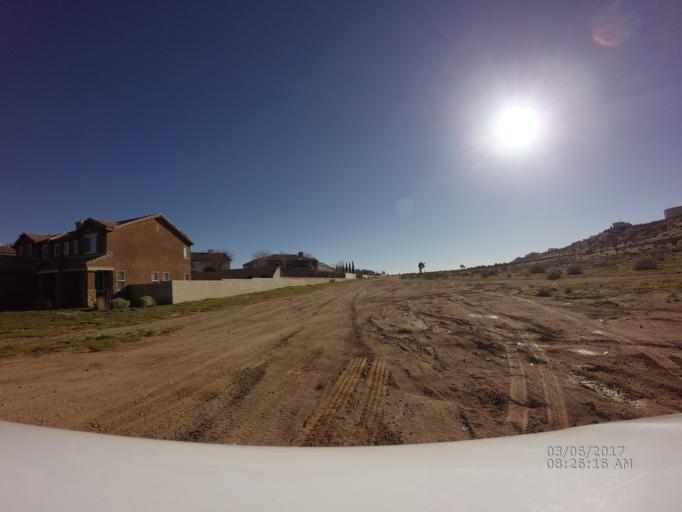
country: US
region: California
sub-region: Los Angeles County
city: Quartz Hill
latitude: 34.6491
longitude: -118.2056
